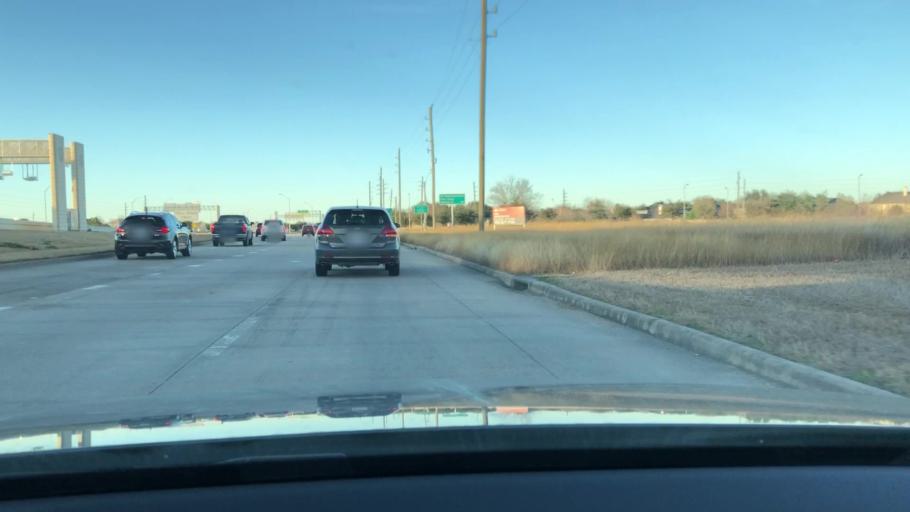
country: US
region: Texas
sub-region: Fort Bend County
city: Cinco Ranch
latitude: 29.7034
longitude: -95.7757
